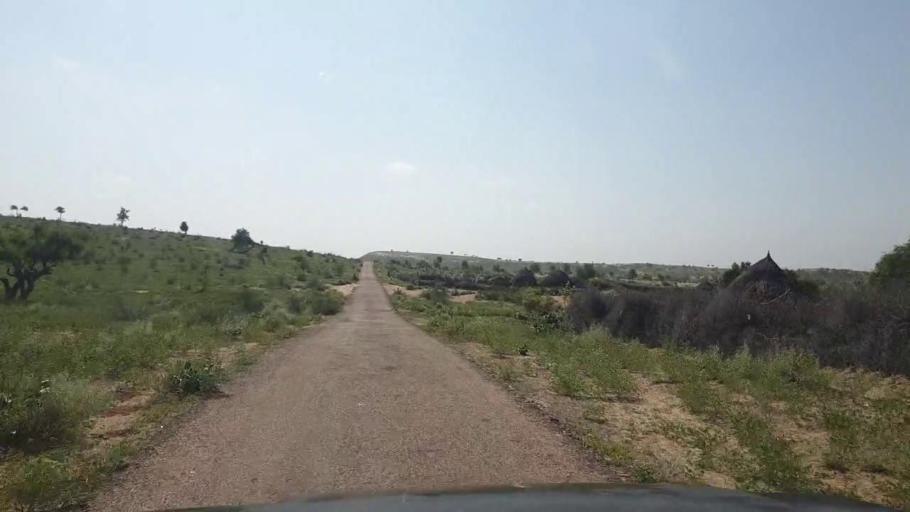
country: PK
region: Sindh
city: Islamkot
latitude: 25.1687
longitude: 70.4008
